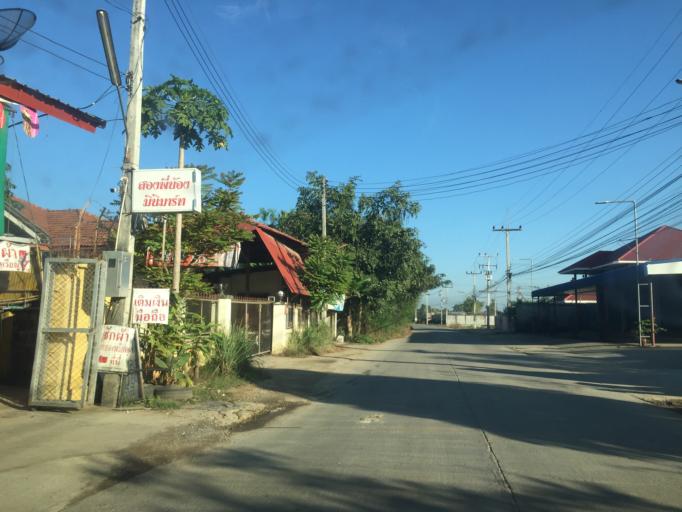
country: TH
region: Lamphun
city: Lamphun
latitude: 18.6114
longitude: 99.0565
